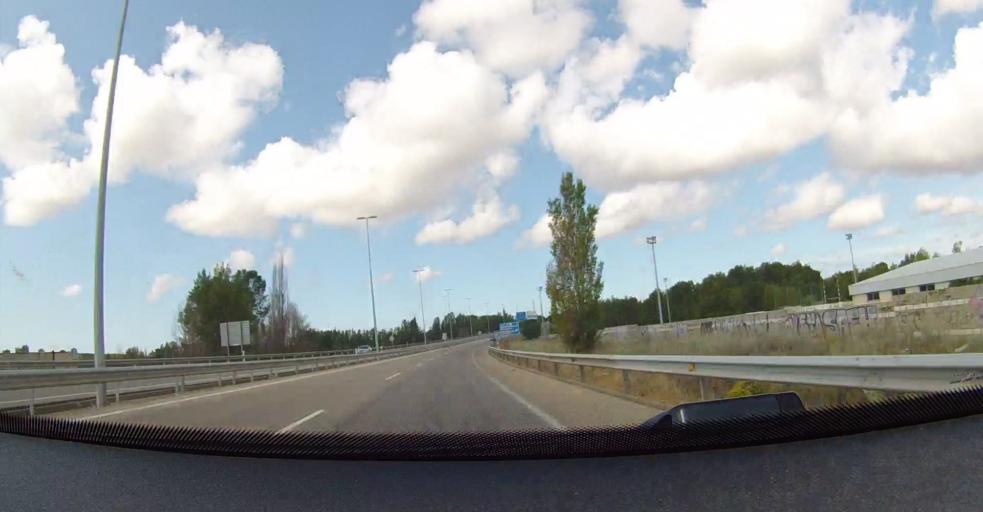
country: ES
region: Castille and Leon
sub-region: Provincia de Leon
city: Leon
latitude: 42.5735
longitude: -5.5622
